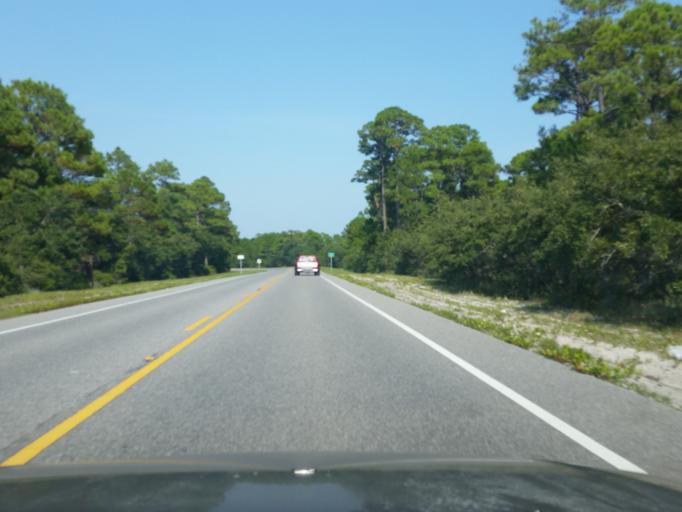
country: US
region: Alabama
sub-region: Baldwin County
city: Gulf Shores
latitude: 30.2396
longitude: -87.8514
